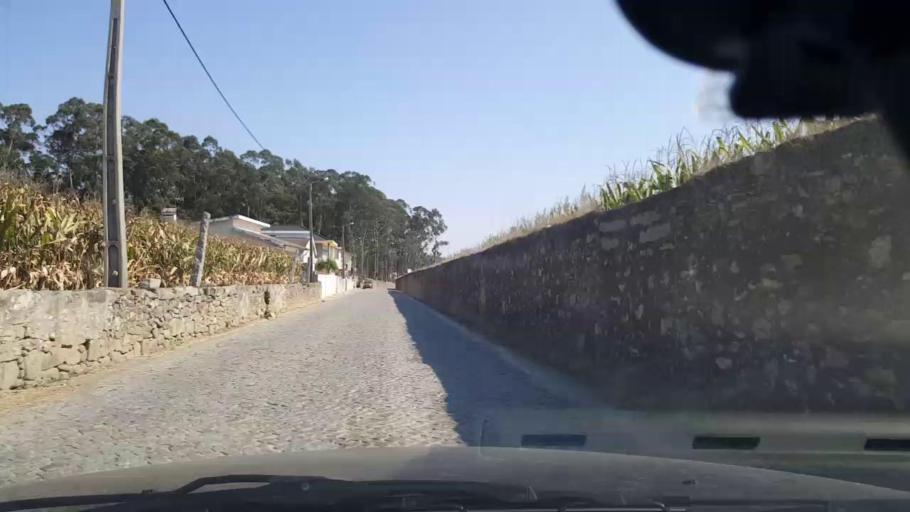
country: PT
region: Porto
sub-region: Povoa de Varzim
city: Pedroso
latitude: 41.4047
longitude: -8.6897
